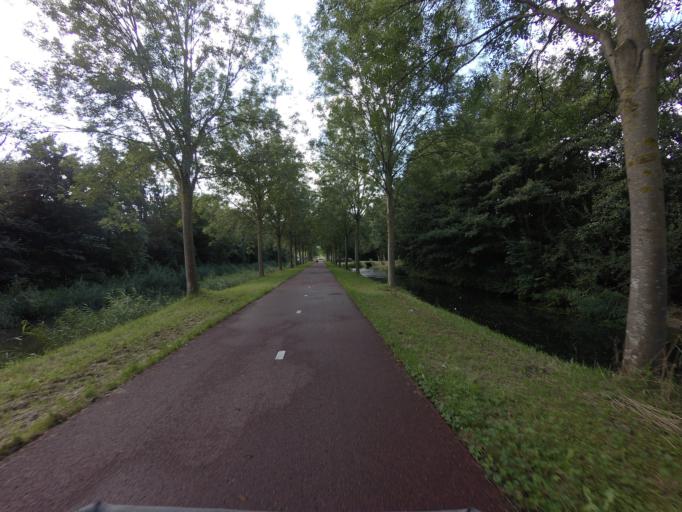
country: NL
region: North Holland
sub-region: Gemeente Edam-Volendam
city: Edam
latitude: 52.5150
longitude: 5.0042
